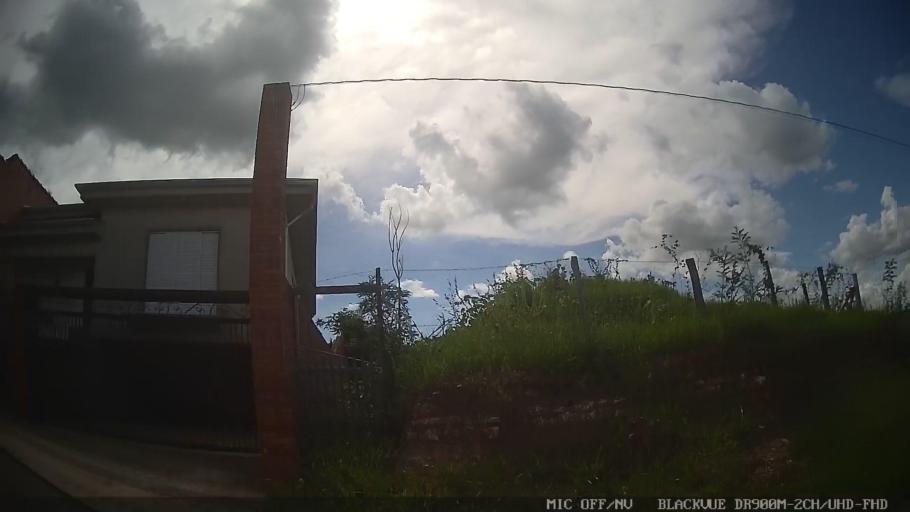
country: BR
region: Sao Paulo
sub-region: Conchas
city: Conchas
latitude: -23.0220
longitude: -48.0104
